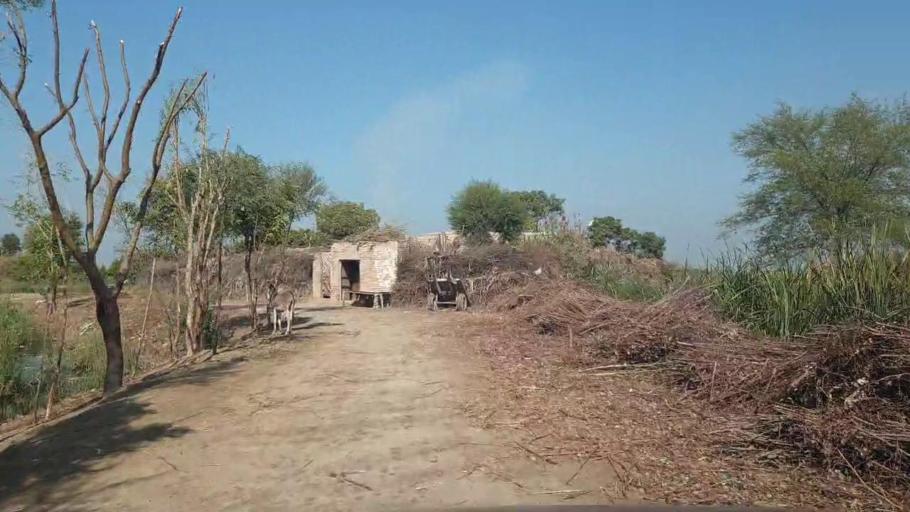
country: PK
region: Sindh
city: Shahdadpur
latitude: 25.9107
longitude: 68.5825
